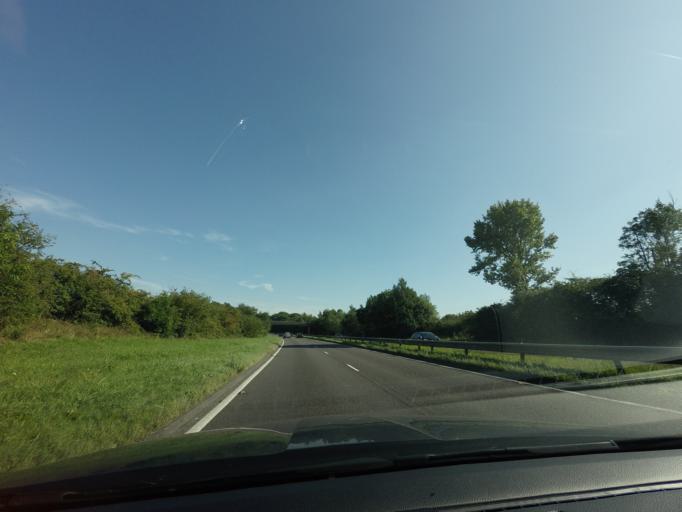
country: GB
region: England
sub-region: Derbyshire
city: Chesterfield
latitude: 53.2146
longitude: -1.3933
